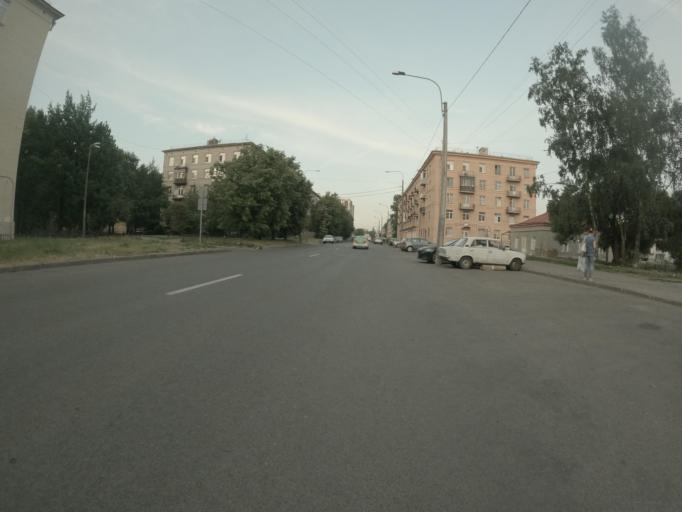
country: RU
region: Leningrad
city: Finlyandskiy
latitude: 59.9710
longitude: 30.3889
